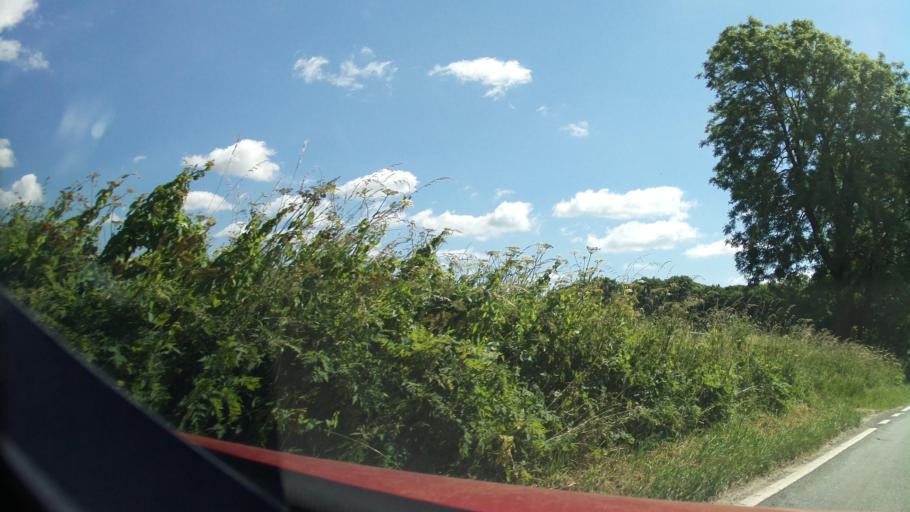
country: GB
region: England
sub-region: Derbyshire
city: Ashbourne
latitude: 53.1229
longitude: -1.7525
